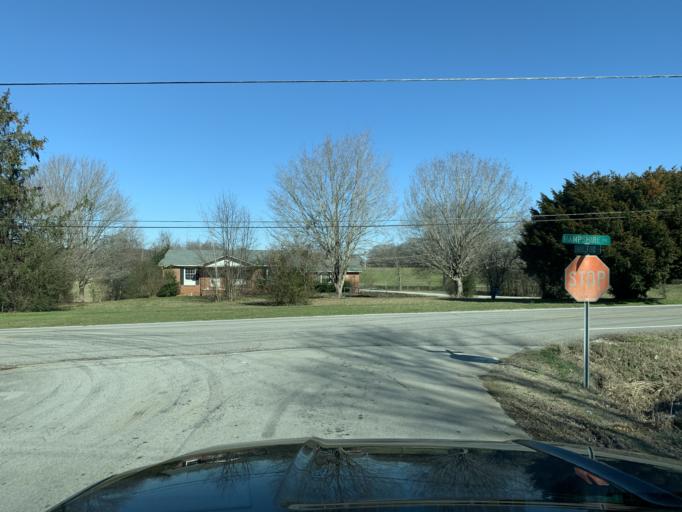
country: US
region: Tennessee
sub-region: Maury County
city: Mount Pleasant
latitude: 35.5444
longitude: -87.2284
